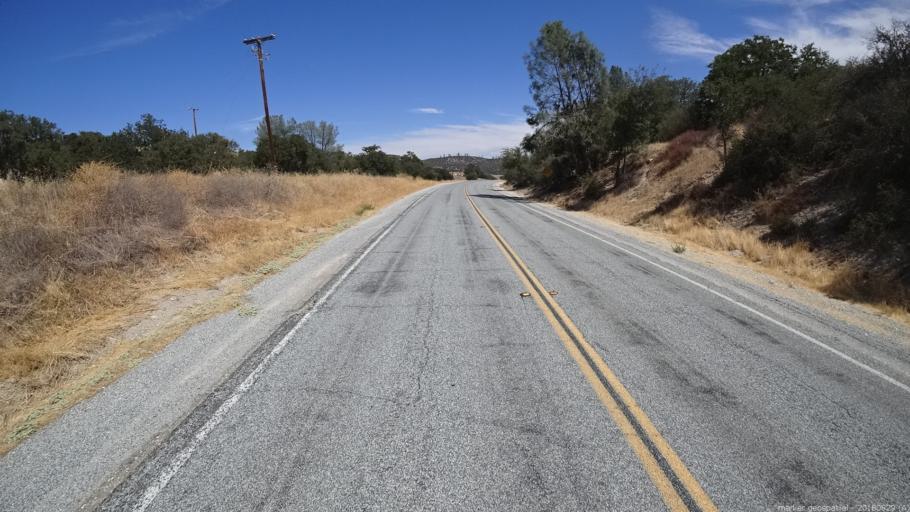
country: US
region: California
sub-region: San Luis Obispo County
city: Lake Nacimiento
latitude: 35.9064
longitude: -120.9935
